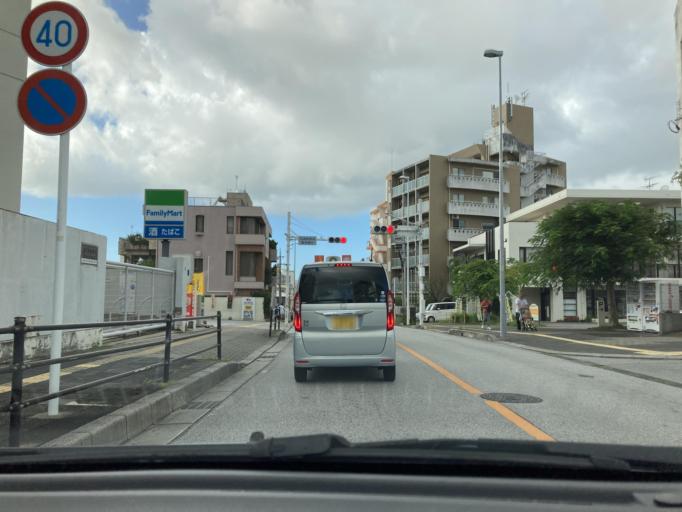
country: JP
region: Okinawa
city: Naha-shi
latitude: 26.2125
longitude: 127.6855
